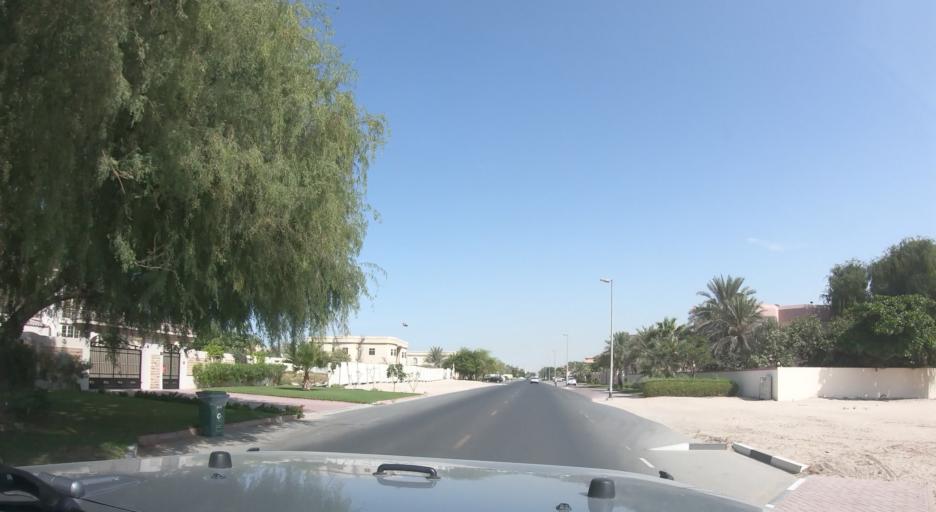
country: AE
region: Dubai
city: Dubai
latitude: 25.1576
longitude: 55.2223
